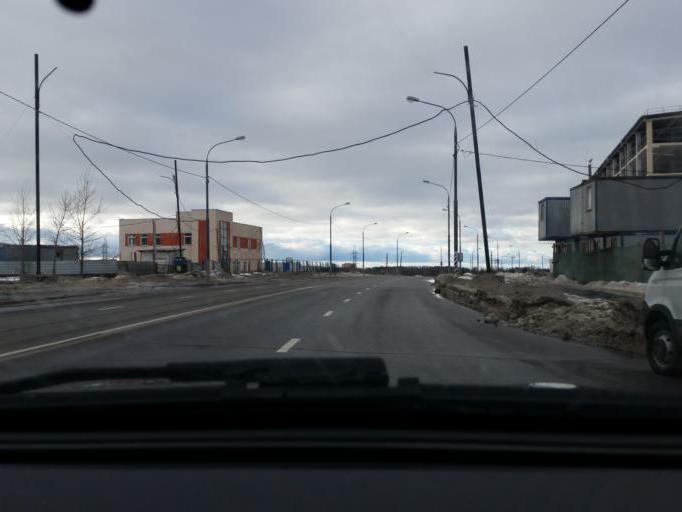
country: RU
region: Moskovskaya
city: Shcherbinka
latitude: 55.5018
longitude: 37.6024
